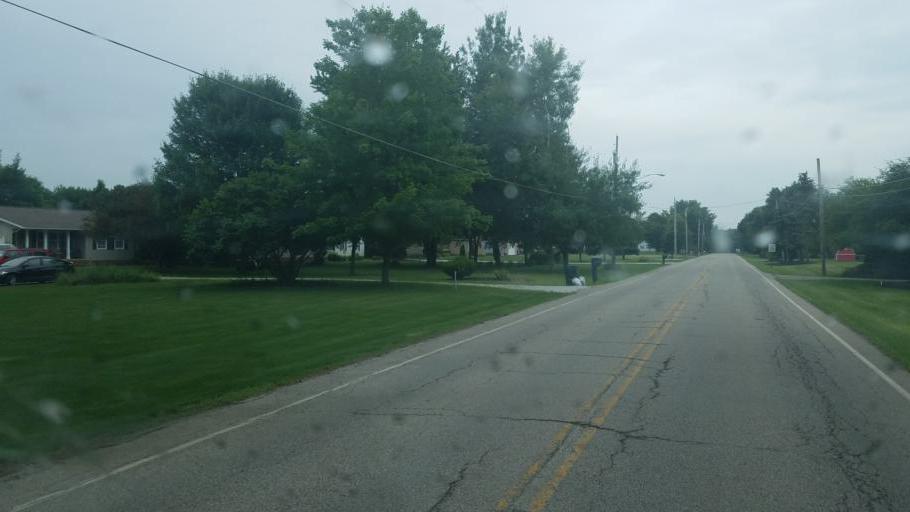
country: US
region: Ohio
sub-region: Summit County
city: Clinton
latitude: 40.9241
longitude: -81.6283
